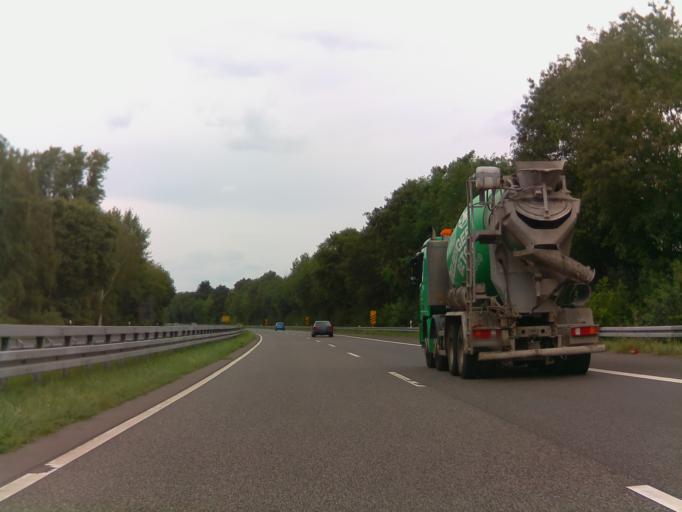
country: DE
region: Hesse
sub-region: Regierungsbezirk Darmstadt
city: Hanau am Main
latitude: 50.0965
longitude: 8.8992
